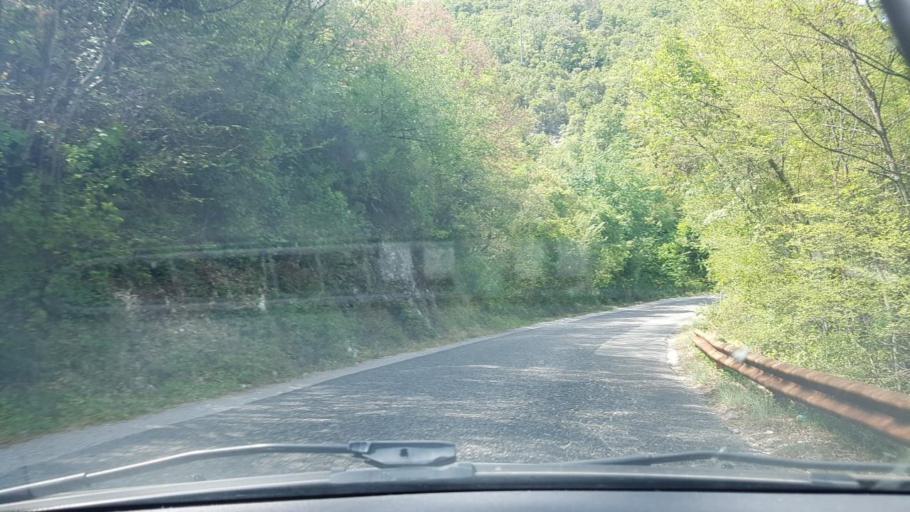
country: BA
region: Federation of Bosnia and Herzegovina
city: Tasovcici
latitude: 43.0101
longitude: 17.7909
